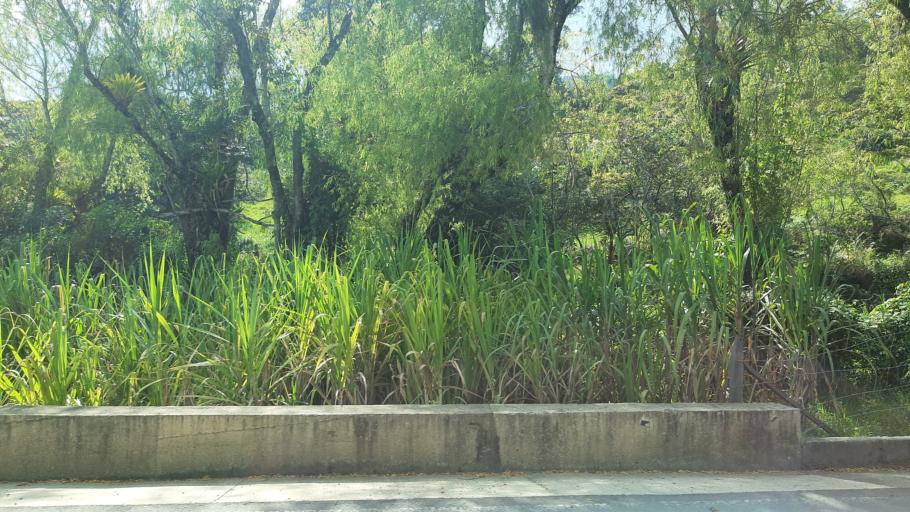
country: CO
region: Boyaca
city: Santa Sofia
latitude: 5.7759
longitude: -73.6055
